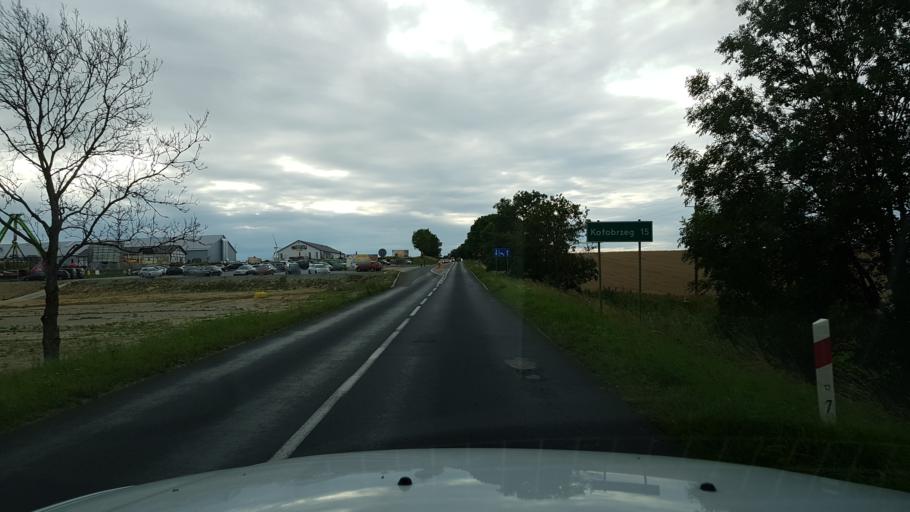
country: PL
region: West Pomeranian Voivodeship
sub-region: Powiat kolobrzeski
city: Dygowo
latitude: 54.1215
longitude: 15.7596
